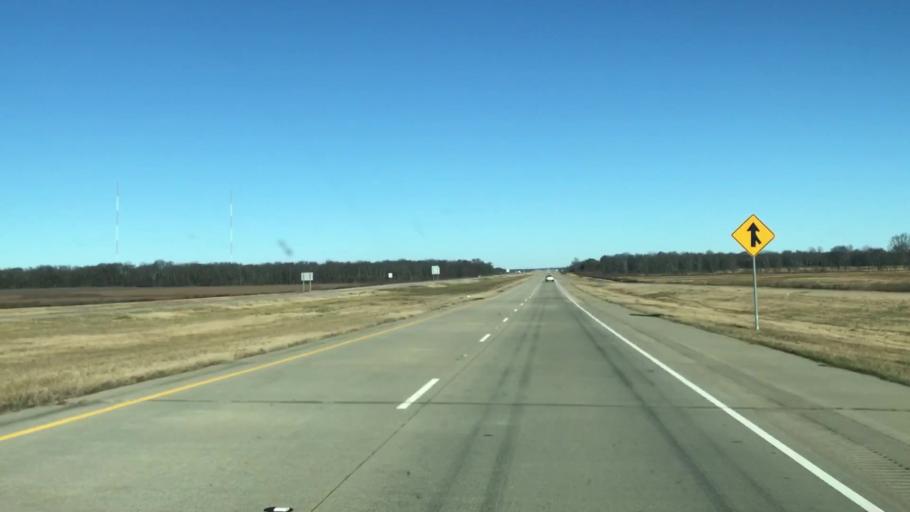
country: US
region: Louisiana
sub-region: Caddo Parish
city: Blanchard
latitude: 32.6776
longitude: -93.8511
